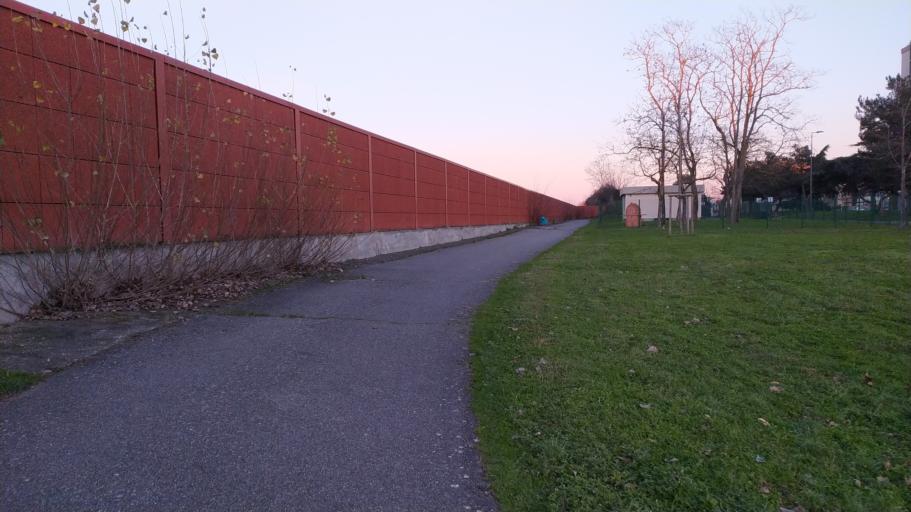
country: FR
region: Midi-Pyrenees
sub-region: Departement de la Haute-Garonne
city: Colomiers
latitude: 43.6066
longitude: 1.3178
